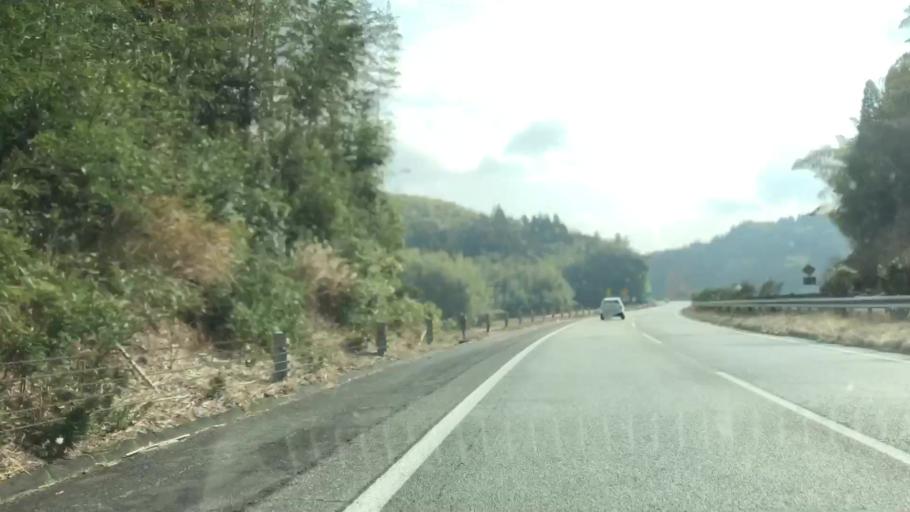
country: JP
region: Kumamoto
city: Yamaga
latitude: 33.0275
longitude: 130.5767
